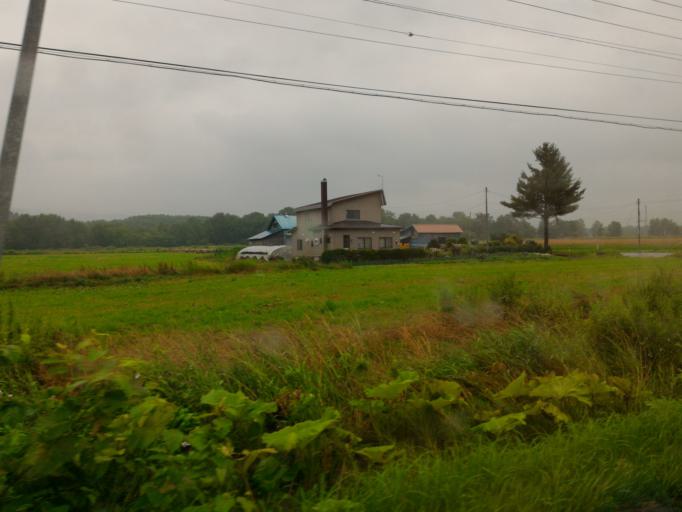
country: JP
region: Hokkaido
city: Nayoro
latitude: 44.5178
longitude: 142.3291
